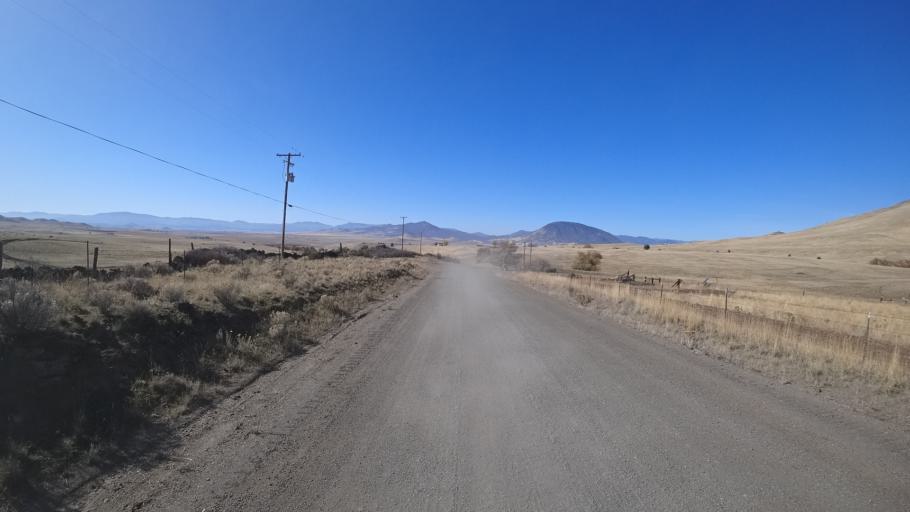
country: US
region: California
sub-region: Siskiyou County
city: Montague
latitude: 41.8323
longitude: -122.3809
